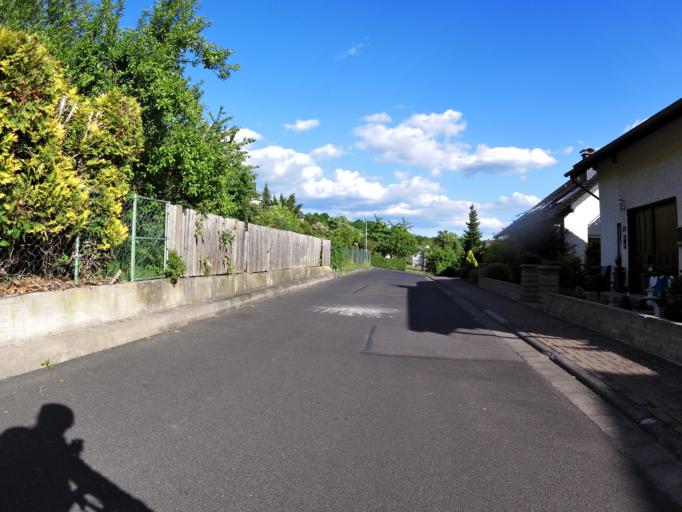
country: DE
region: Hesse
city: Philippsthal
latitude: 50.8378
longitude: 10.0128
